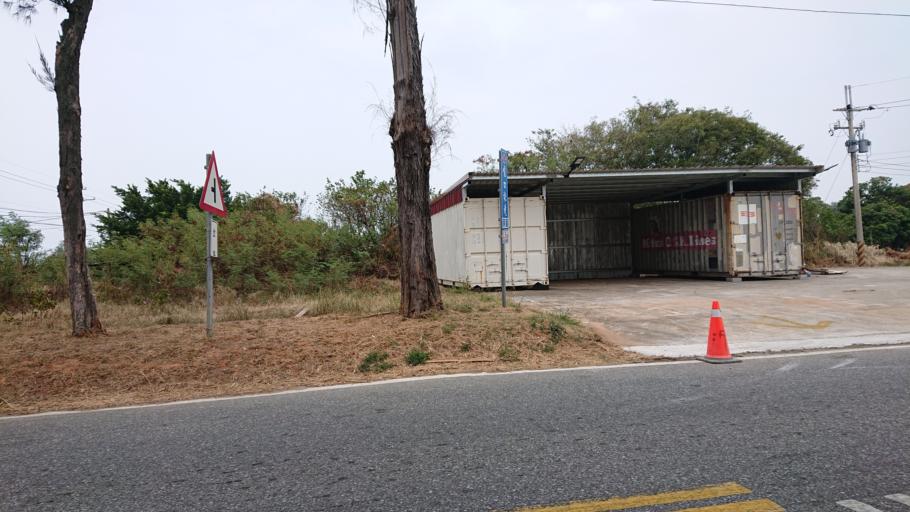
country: TW
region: Fukien
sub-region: Kinmen
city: Jincheng
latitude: 24.4588
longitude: 118.3624
